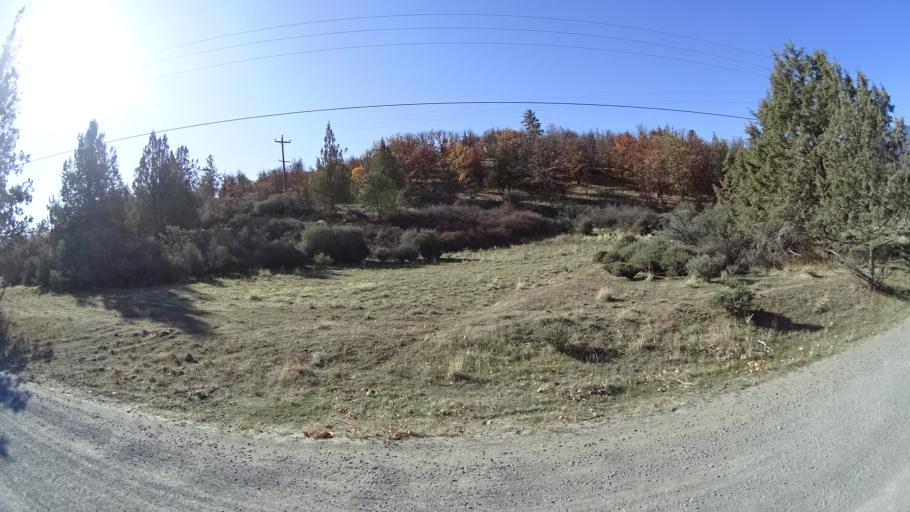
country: US
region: California
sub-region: Siskiyou County
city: Montague
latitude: 41.8987
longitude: -122.5103
